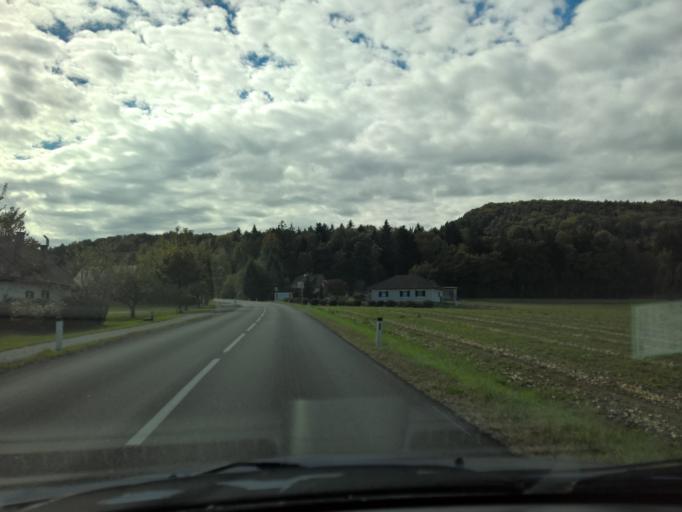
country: AT
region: Styria
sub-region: Politischer Bezirk Leibnitz
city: Heimschuh
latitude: 46.7498
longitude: 15.4738
